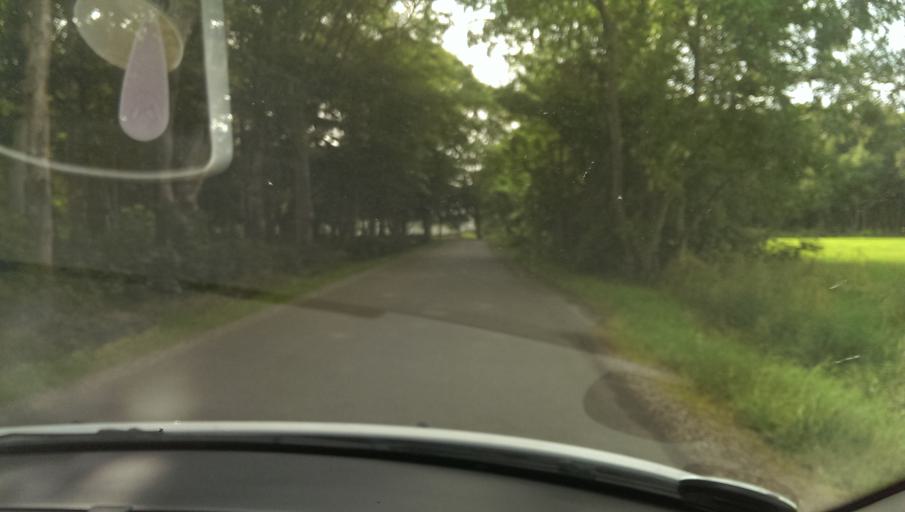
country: DK
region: Central Jutland
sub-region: Holstebro Kommune
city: Ulfborg
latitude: 56.2779
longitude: 8.2386
